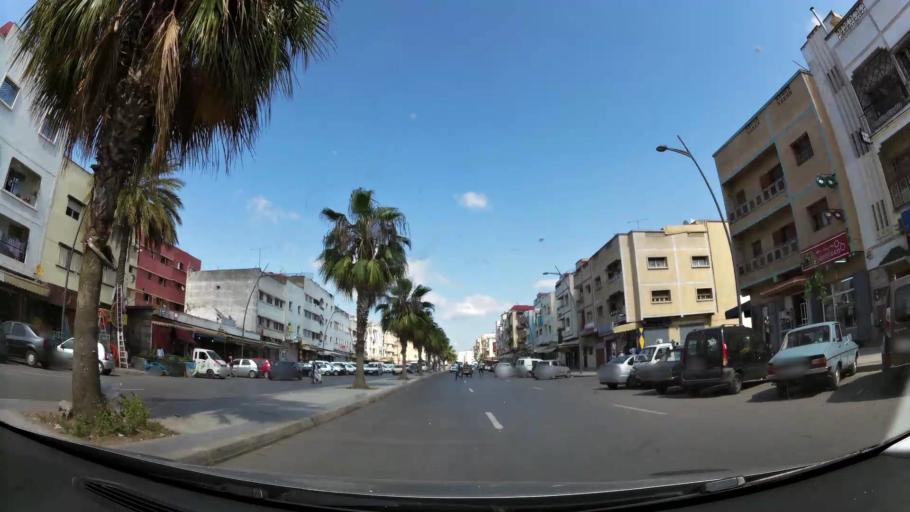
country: MA
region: Rabat-Sale-Zemmour-Zaer
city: Sale
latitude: 34.0471
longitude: -6.7803
